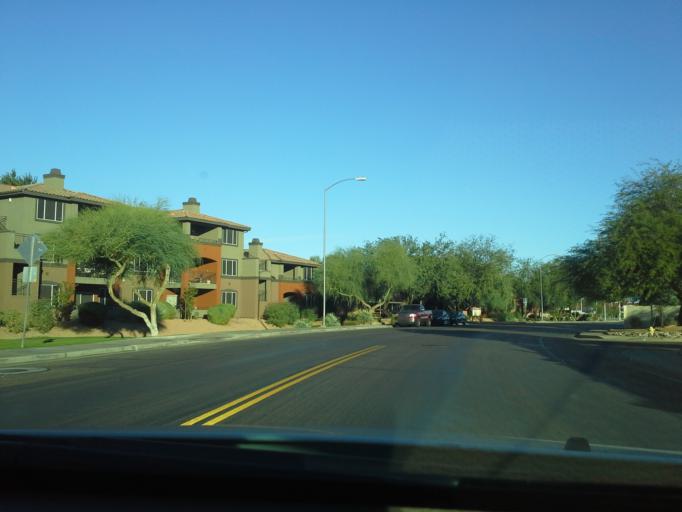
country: US
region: Arizona
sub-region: Maricopa County
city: Tempe
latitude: 33.4279
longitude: -111.8800
